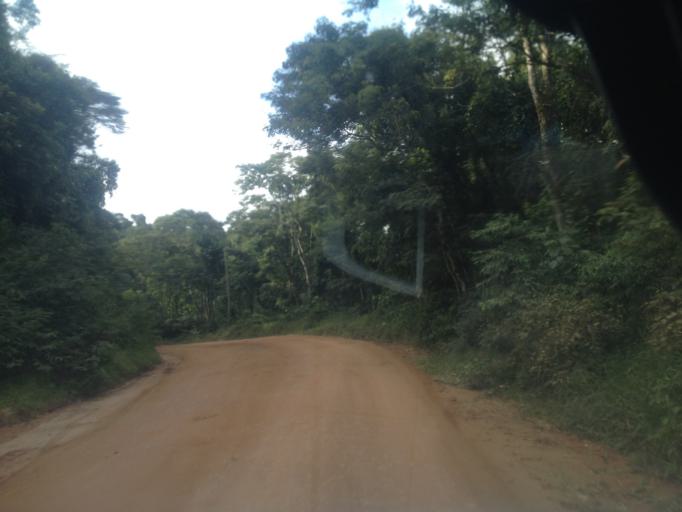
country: BR
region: Rio de Janeiro
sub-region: Quatis
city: Quatis
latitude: -22.2341
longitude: -44.2590
